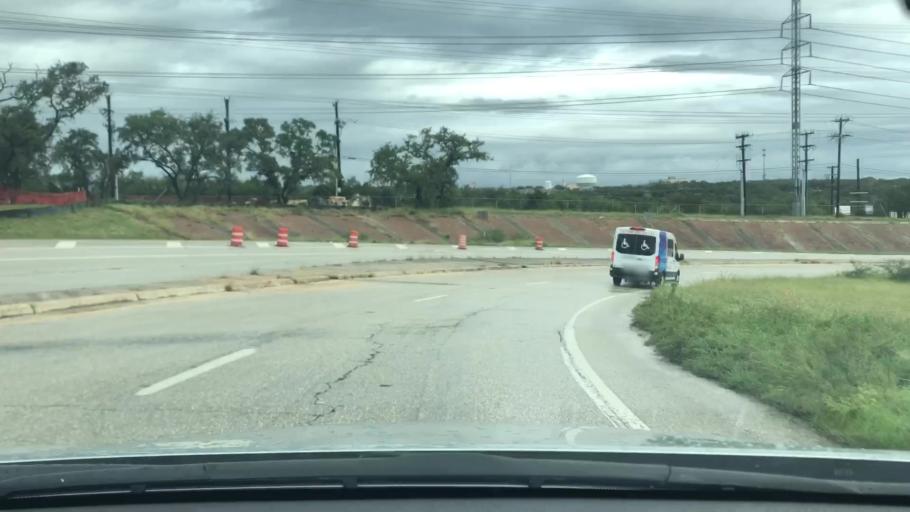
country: US
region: Texas
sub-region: Bexar County
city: Hollywood Park
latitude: 29.6151
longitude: -98.4684
